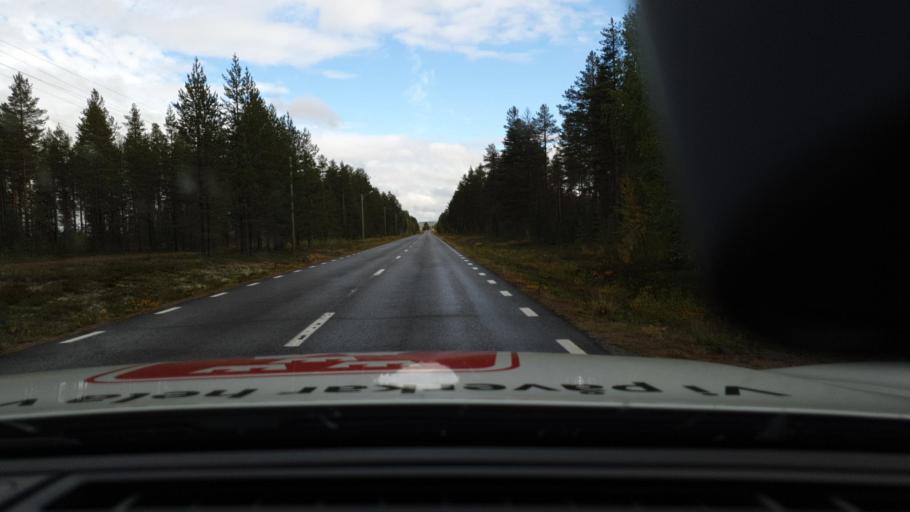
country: SE
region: Norrbotten
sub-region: Overkalix Kommun
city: OEverkalix
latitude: 66.9449
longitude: 22.7198
